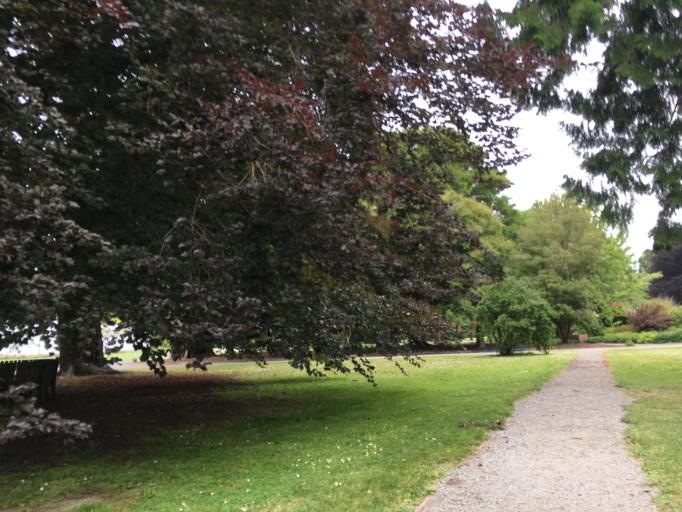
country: NZ
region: Canterbury
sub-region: Christchurch City
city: Christchurch
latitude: -43.5297
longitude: 172.6214
